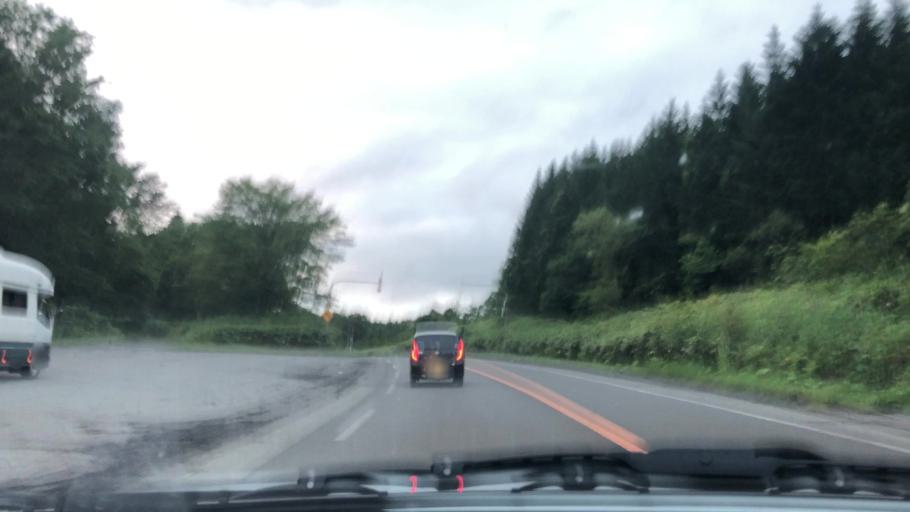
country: JP
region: Hokkaido
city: Iwamizawa
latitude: 42.9174
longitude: 142.1200
